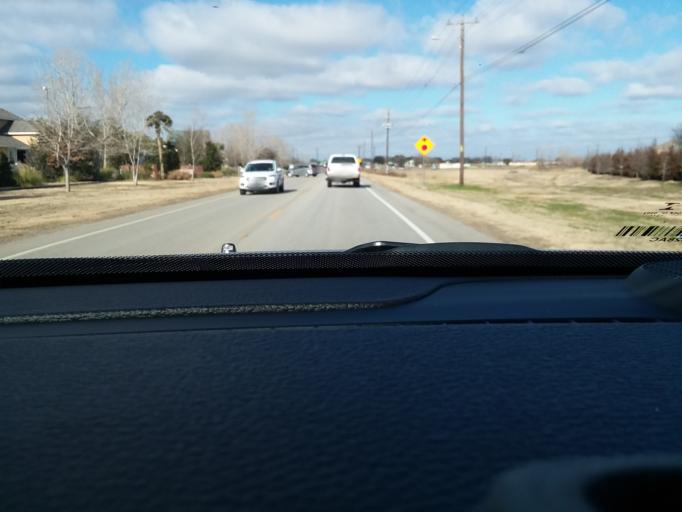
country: US
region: Texas
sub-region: Denton County
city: Little Elm
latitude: 33.2279
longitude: -96.8971
